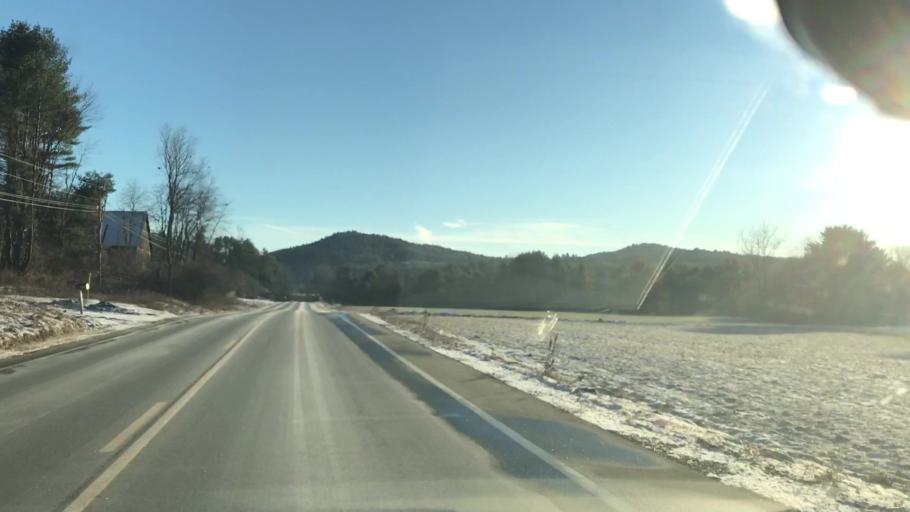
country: US
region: New Hampshire
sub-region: Grafton County
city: Lyme Town Offices
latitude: 43.8533
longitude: -72.1559
